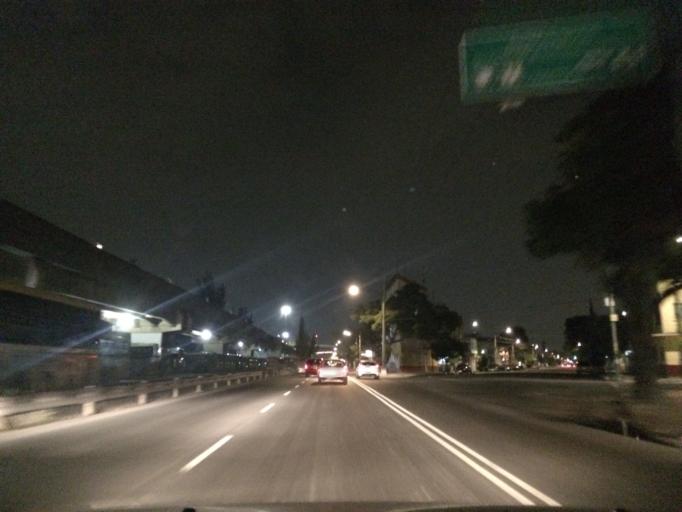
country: MX
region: Mexico City
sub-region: Iztacalco
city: Iztacalco
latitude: 19.4079
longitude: -99.0863
